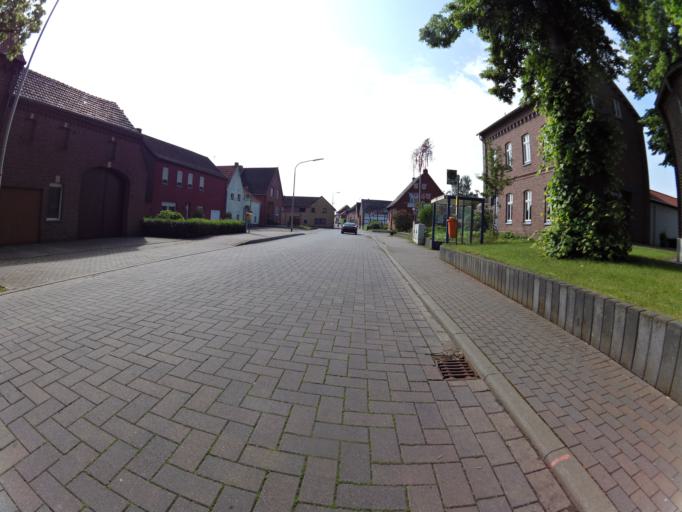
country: DE
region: North Rhine-Westphalia
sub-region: Regierungsbezirk Koln
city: Waldfeucht
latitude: 51.0740
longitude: 5.9970
